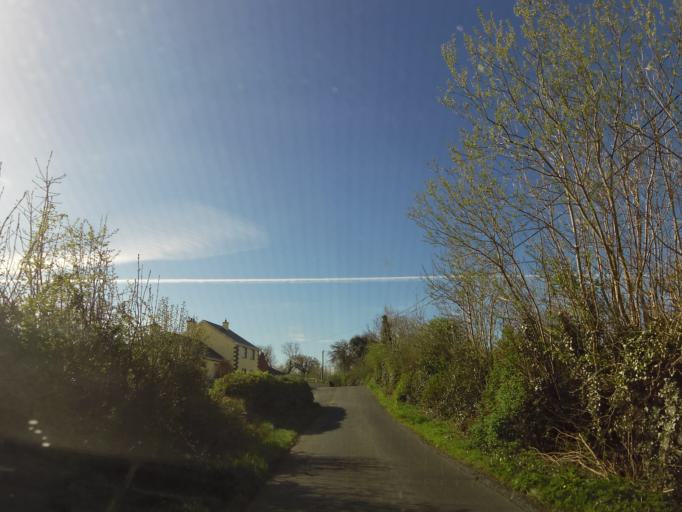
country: IE
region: Connaught
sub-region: Maigh Eo
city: Kiltamagh
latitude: 53.7872
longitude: -8.9626
